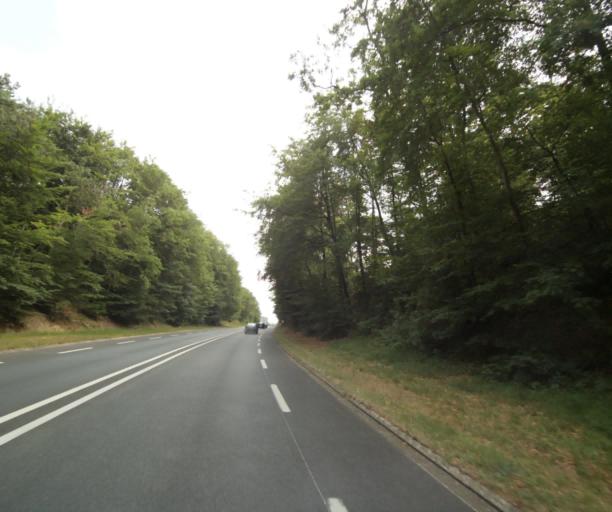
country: FR
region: Ile-de-France
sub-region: Departement de Seine-et-Marne
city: Fontainebleau
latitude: 48.4309
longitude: 2.7013
